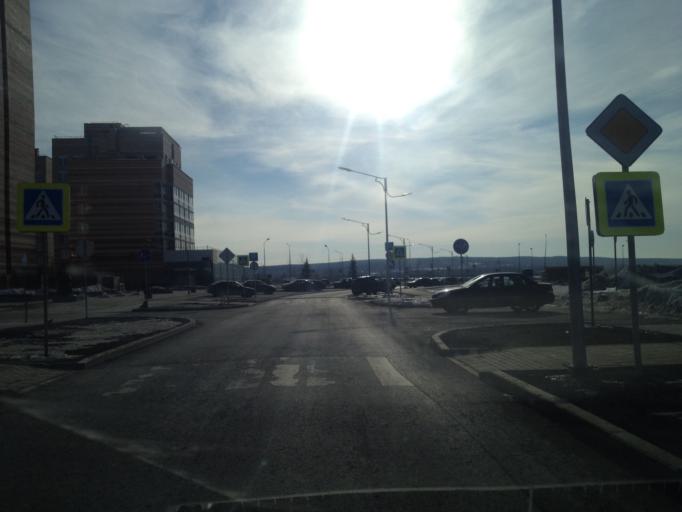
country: RU
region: Sverdlovsk
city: Sovkhoznyy
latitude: 56.7457
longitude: 60.5676
